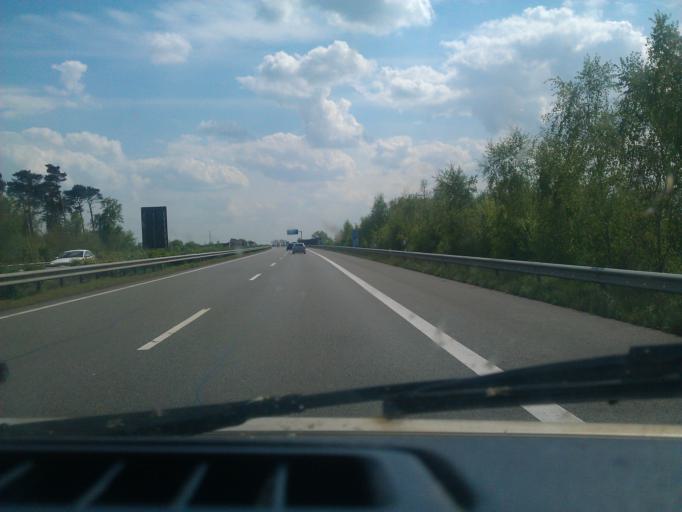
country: DE
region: Lower Saxony
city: Schuttorf
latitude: 52.3287
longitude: 7.2572
